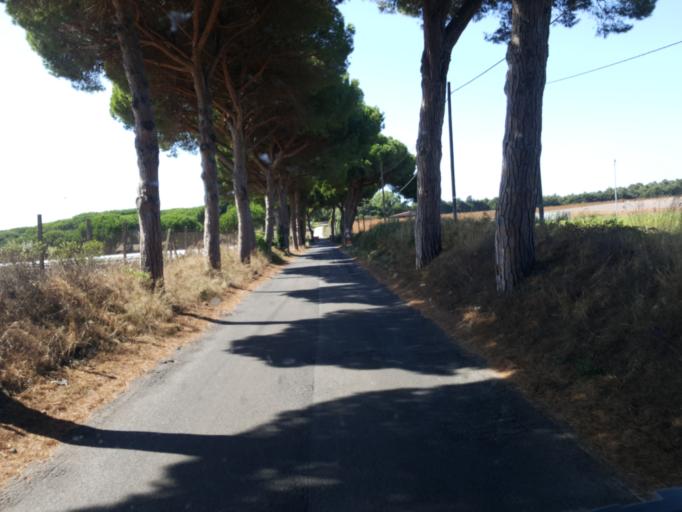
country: IT
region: Latium
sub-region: Citta metropolitana di Roma Capitale
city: Nettuno
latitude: 41.5109
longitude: 12.6551
